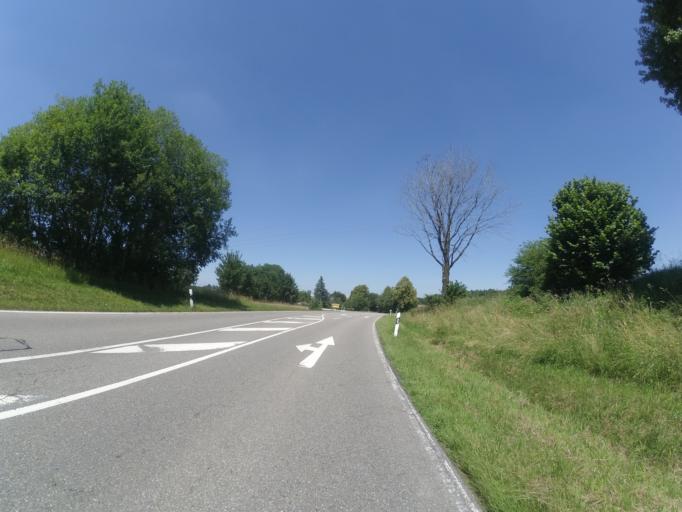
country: DE
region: Baden-Wuerttemberg
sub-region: Tuebingen Region
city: Bad Waldsee
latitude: 47.9148
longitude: 9.7659
